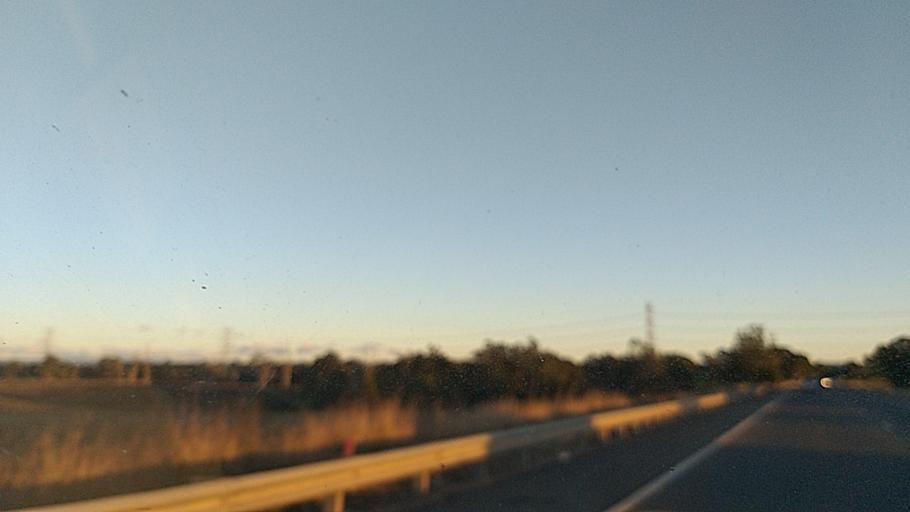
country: AU
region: New South Wales
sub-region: Blacktown
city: Riverstone
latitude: -33.6798
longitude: 150.8147
